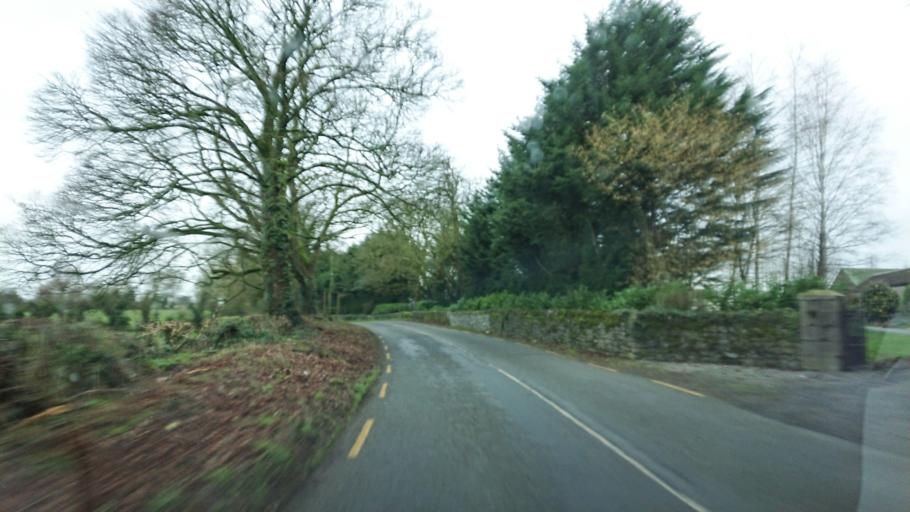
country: IE
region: Leinster
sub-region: Kilkenny
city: Callan
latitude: 52.5365
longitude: -7.2920
